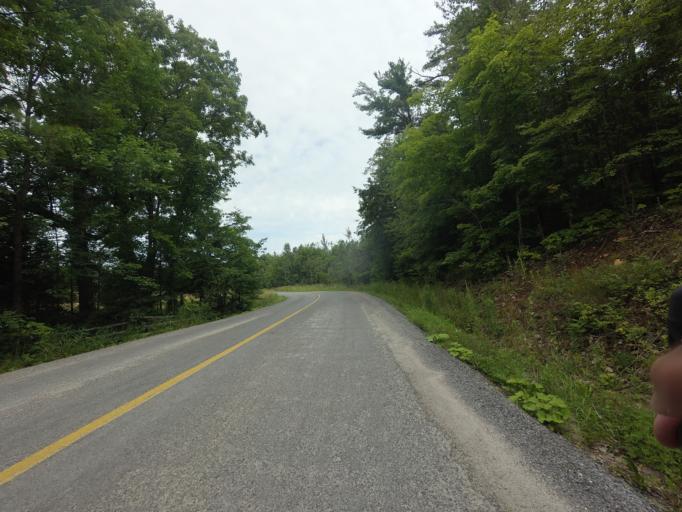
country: CA
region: Ontario
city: Perth
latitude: 44.6682
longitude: -76.6587
